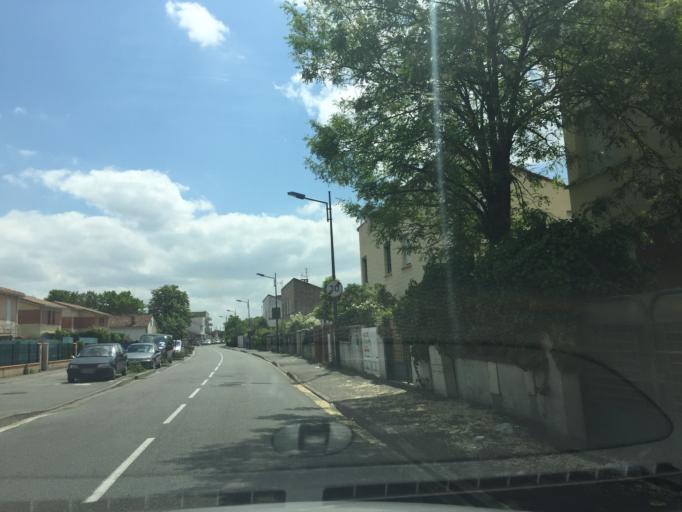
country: FR
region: Midi-Pyrenees
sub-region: Departement de la Haute-Garonne
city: Aucamville
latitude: 43.6417
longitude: 1.4445
